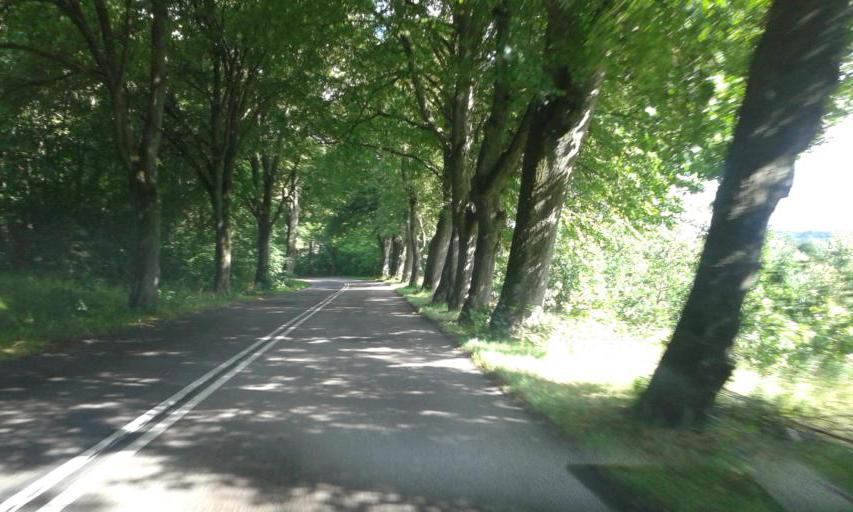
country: PL
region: West Pomeranian Voivodeship
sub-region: Powiat koszalinski
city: Bobolice
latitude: 53.9943
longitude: 16.7001
